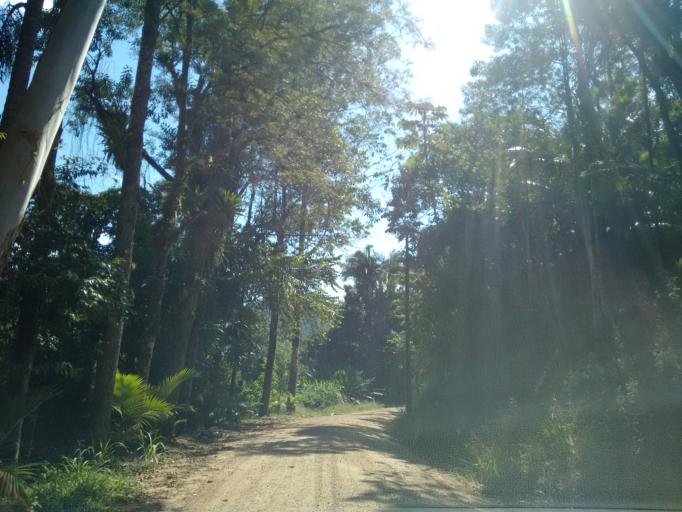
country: BR
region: Santa Catarina
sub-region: Indaial
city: Indaial
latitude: -26.9391
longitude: -49.1784
